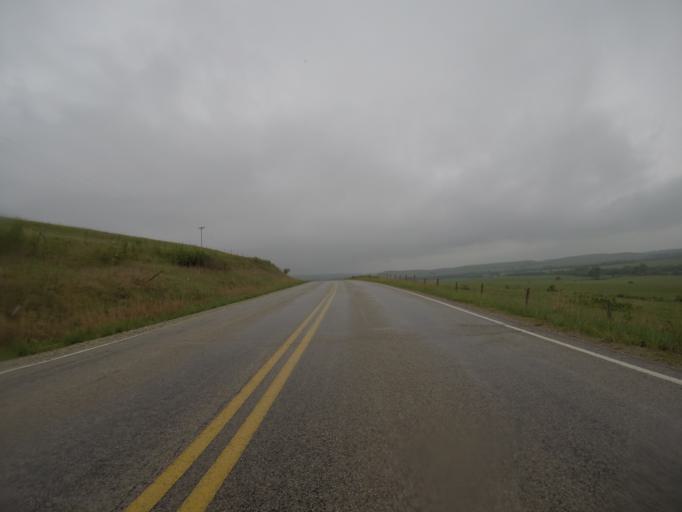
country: US
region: Kansas
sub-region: Pottawatomie County
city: Westmoreland
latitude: 39.4164
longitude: -96.1844
